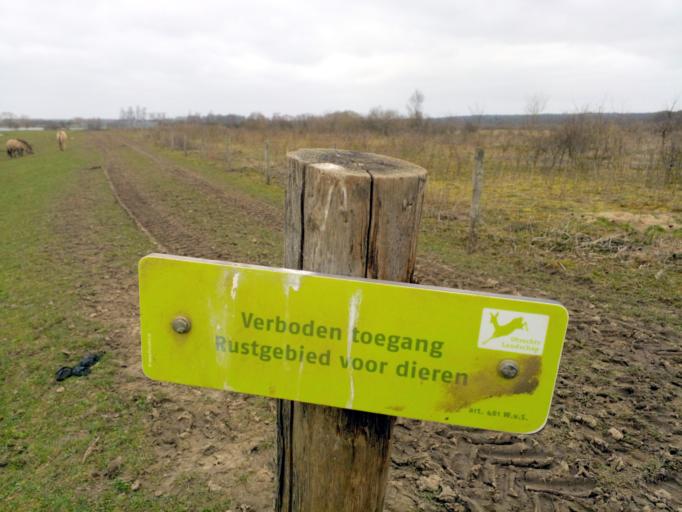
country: NL
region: Utrecht
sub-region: Gemeente Utrechtse Heuvelrug
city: Amerongen
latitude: 51.9856
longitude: 5.4792
